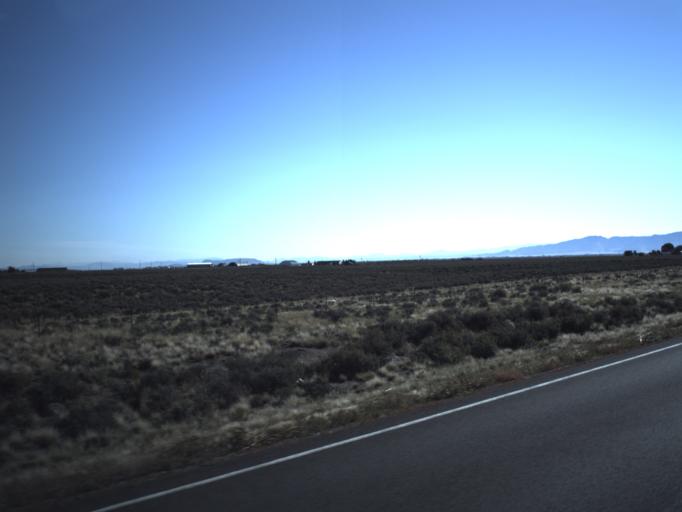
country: US
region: Utah
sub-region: Washington County
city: Enterprise
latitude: 37.7612
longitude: -113.8023
